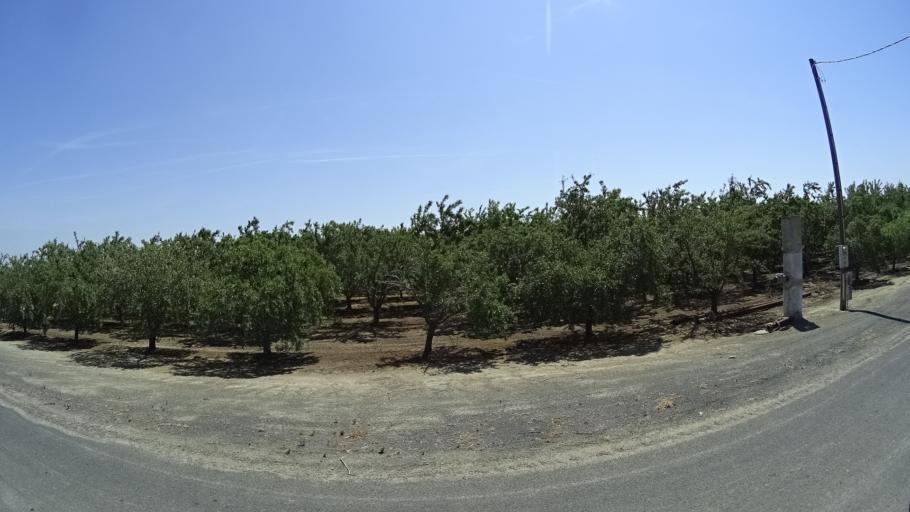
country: US
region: California
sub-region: Fresno County
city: Riverdale
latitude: 36.3889
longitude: -119.8693
